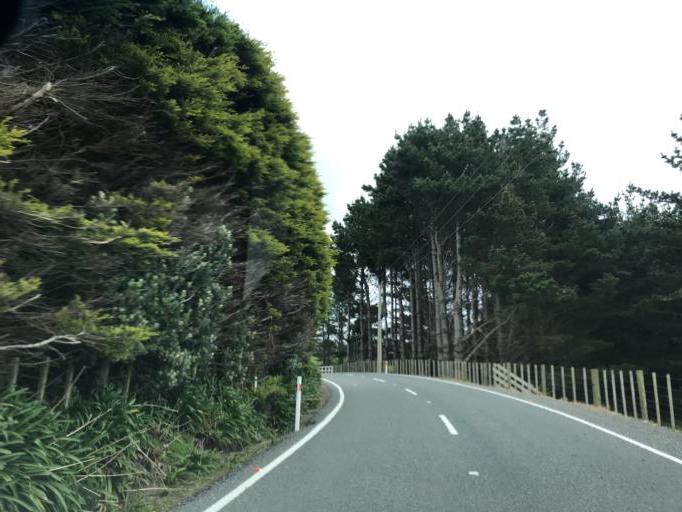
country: NZ
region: Wellington
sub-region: Porirua City
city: Porirua
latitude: -41.1774
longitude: 174.7974
